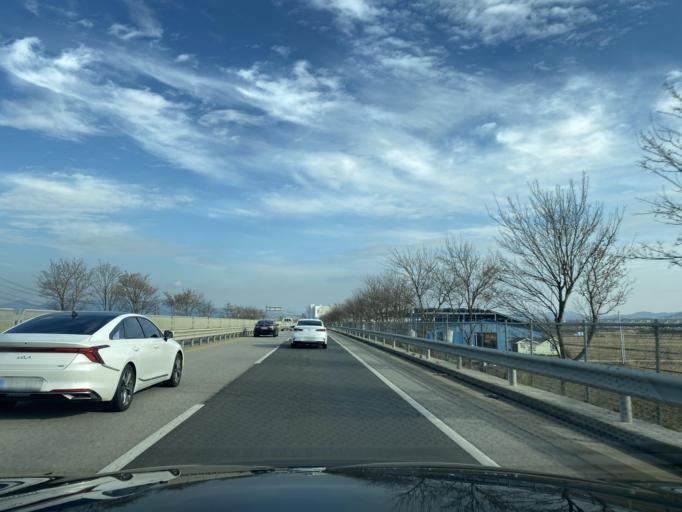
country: KR
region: Chungcheongnam-do
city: Yesan
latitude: 36.6874
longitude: 126.7649
